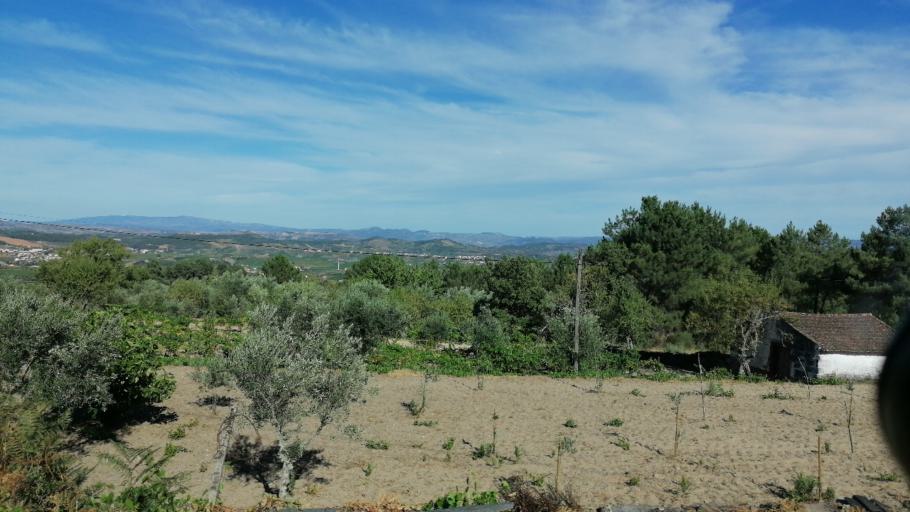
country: PT
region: Vila Real
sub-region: Murca
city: Murca
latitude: 41.4017
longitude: -7.4799
